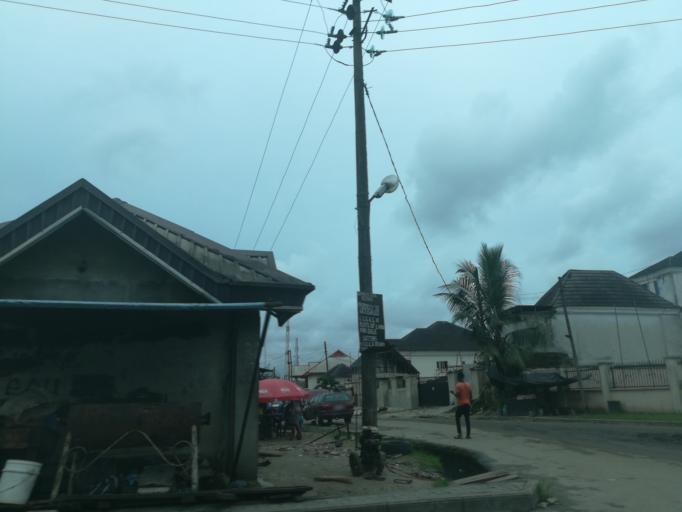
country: NG
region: Rivers
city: Port Harcourt
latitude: 4.8217
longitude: 6.9938
